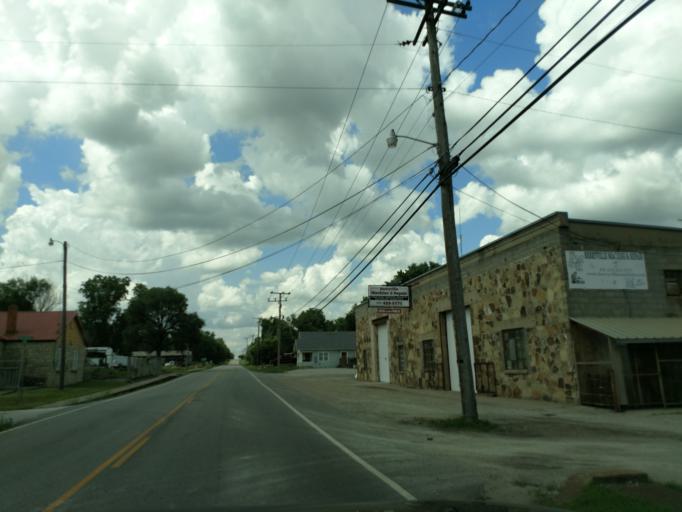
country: US
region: Arkansas
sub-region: Carroll County
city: Berryville
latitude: 36.3713
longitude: -93.5672
